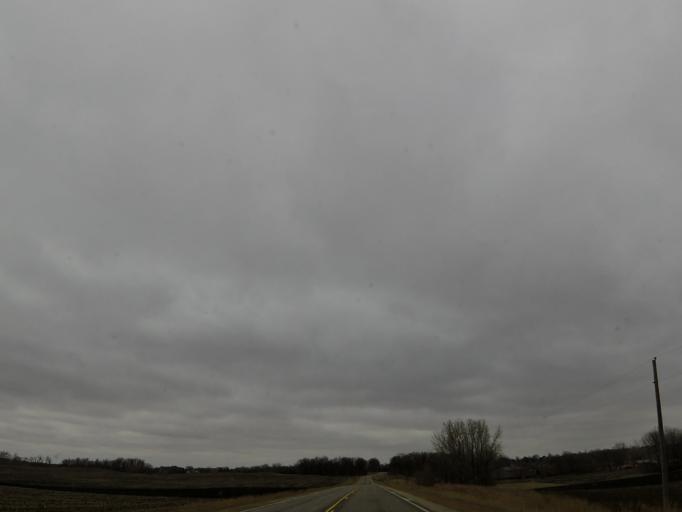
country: US
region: Minnesota
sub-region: Scott County
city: Shakopee
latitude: 44.7249
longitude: -93.5208
